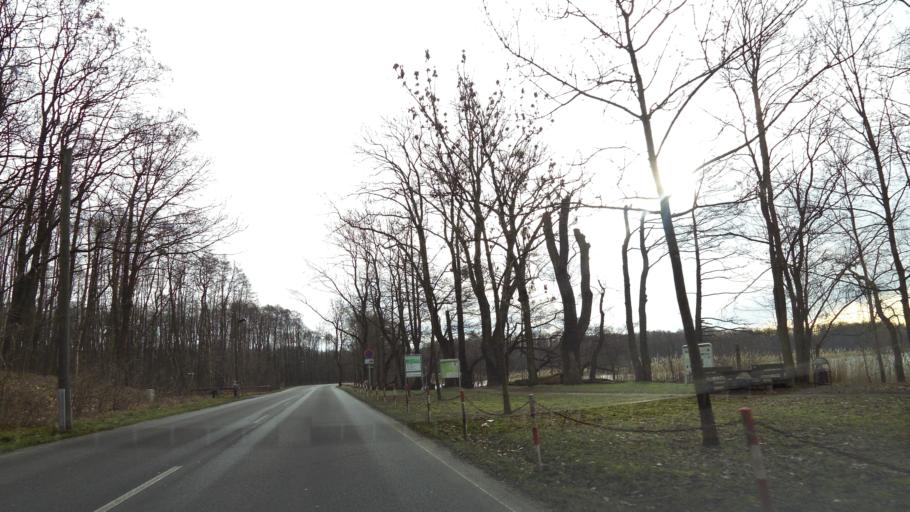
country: DE
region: Brandenburg
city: Strausberg
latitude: 52.5926
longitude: 13.8919
